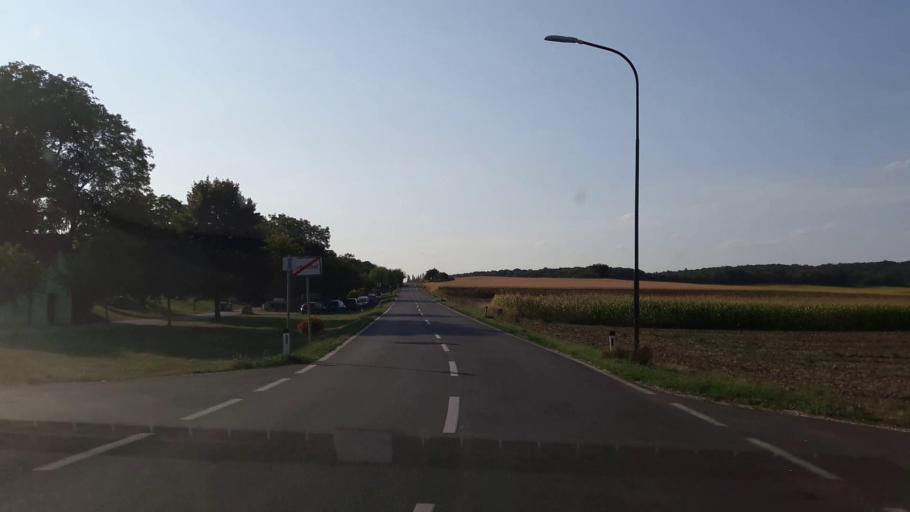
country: AT
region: Lower Austria
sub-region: Politischer Bezirk Ganserndorf
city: Orth an der Donau
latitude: 48.0693
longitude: 16.7013
